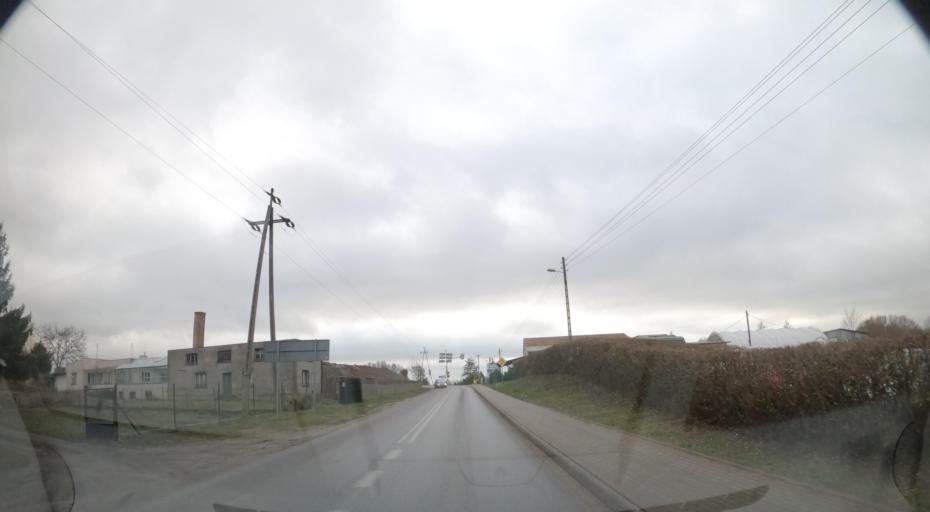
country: PL
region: Greater Poland Voivodeship
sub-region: Powiat pilski
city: Lobzenica
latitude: 53.2593
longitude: 17.2611
